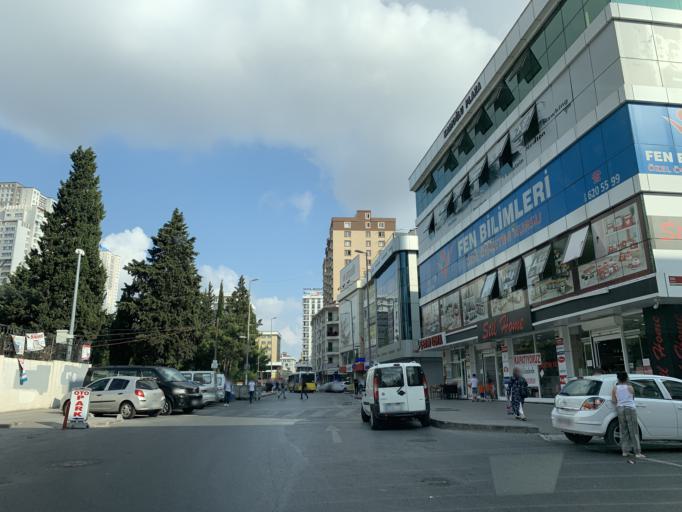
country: TR
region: Istanbul
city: Esenyurt
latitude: 41.0327
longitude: 28.6797
